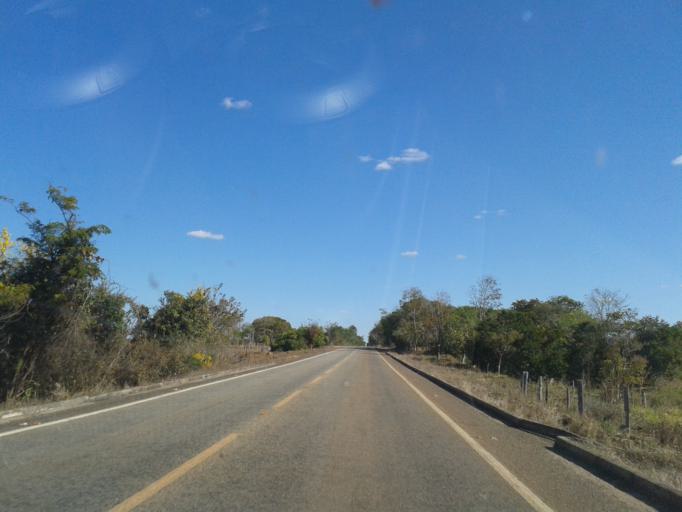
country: BR
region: Goias
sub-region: Mozarlandia
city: Mozarlandia
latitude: -14.5758
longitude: -50.5026
